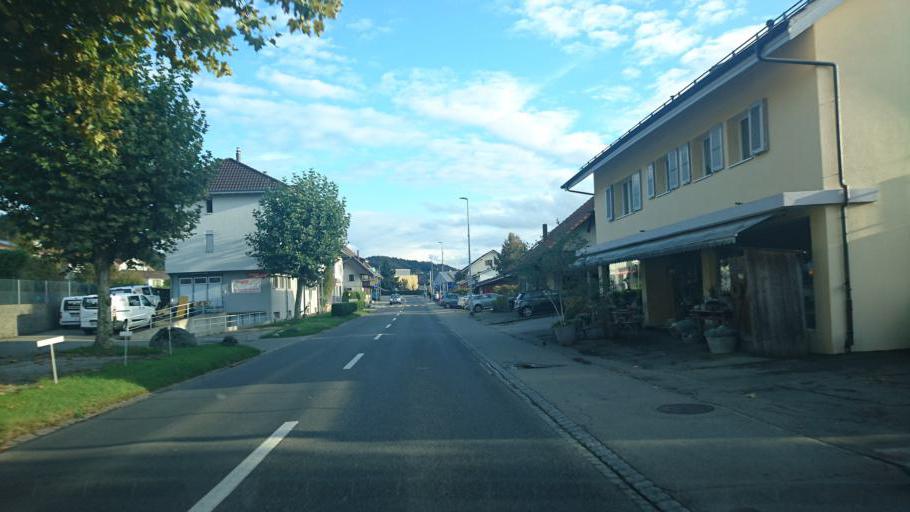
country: CH
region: Bern
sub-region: Bern-Mittelland District
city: Vechigen
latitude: 46.9522
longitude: 7.5494
